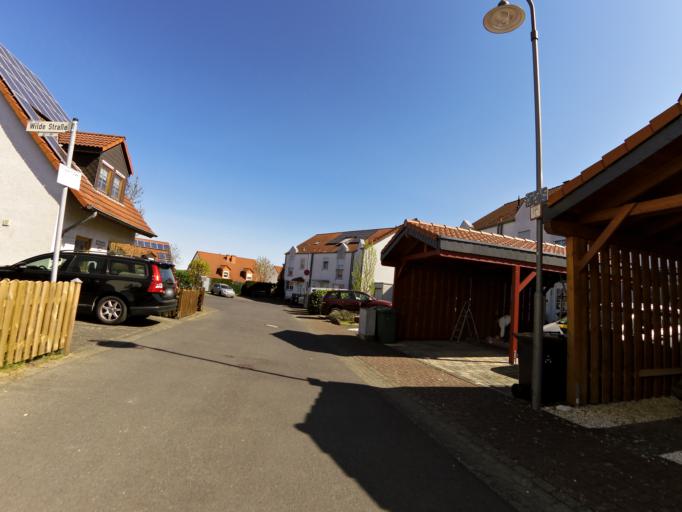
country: DE
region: North Rhine-Westphalia
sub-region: Regierungsbezirk Koln
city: Alfter
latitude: 50.6887
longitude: 7.0203
